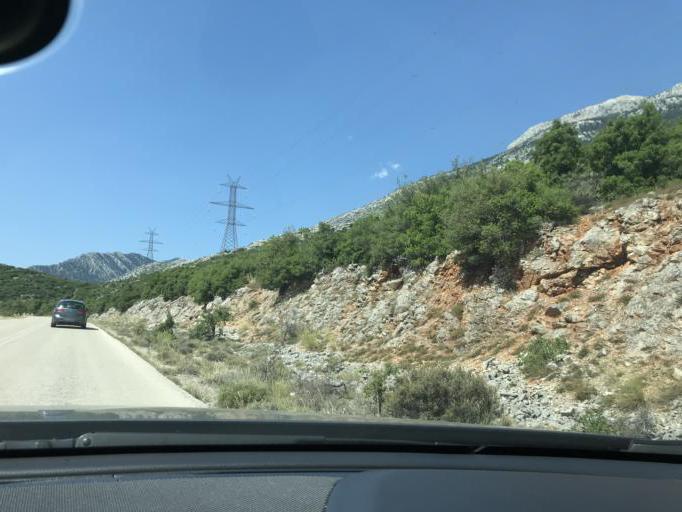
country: GR
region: Central Greece
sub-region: Nomos Voiotias
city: Distomo
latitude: 38.4979
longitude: 22.7001
